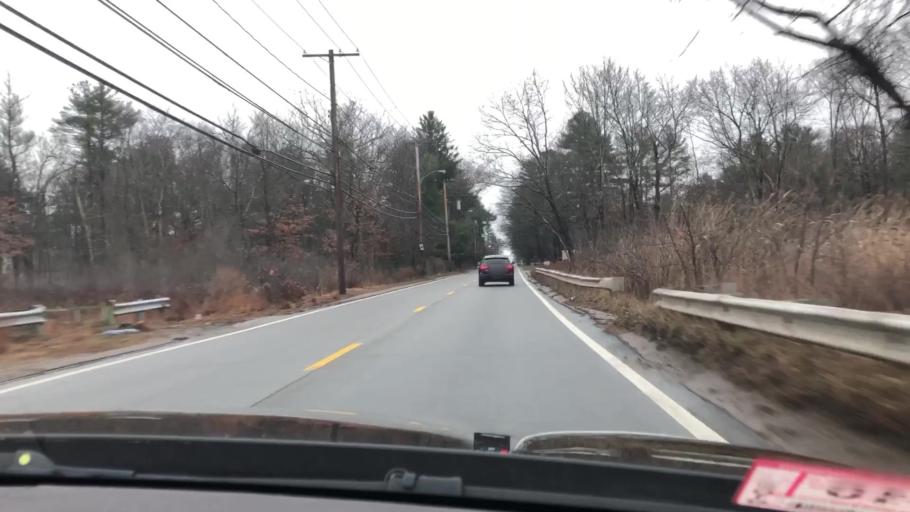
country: US
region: Massachusetts
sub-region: Norfolk County
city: Walpole
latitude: 42.1237
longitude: -71.2715
